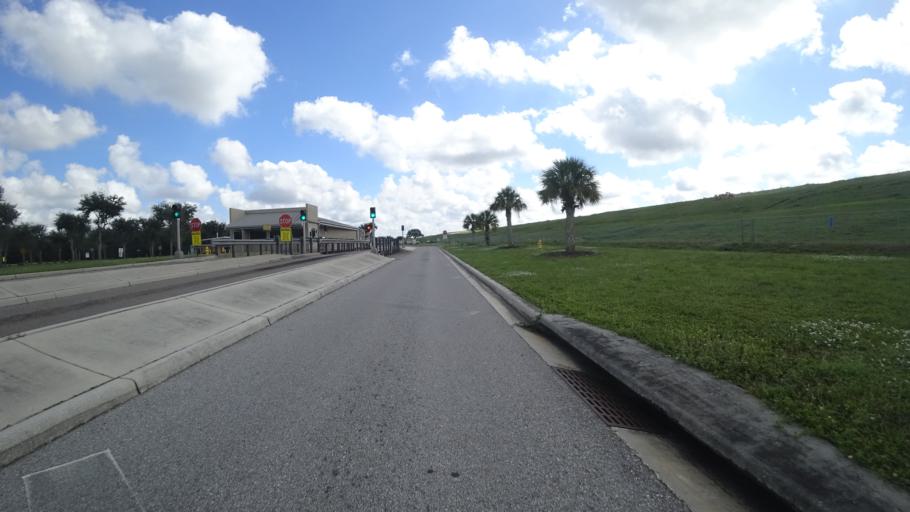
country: US
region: Florida
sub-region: Manatee County
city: Samoset
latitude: 27.4733
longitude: -82.4507
